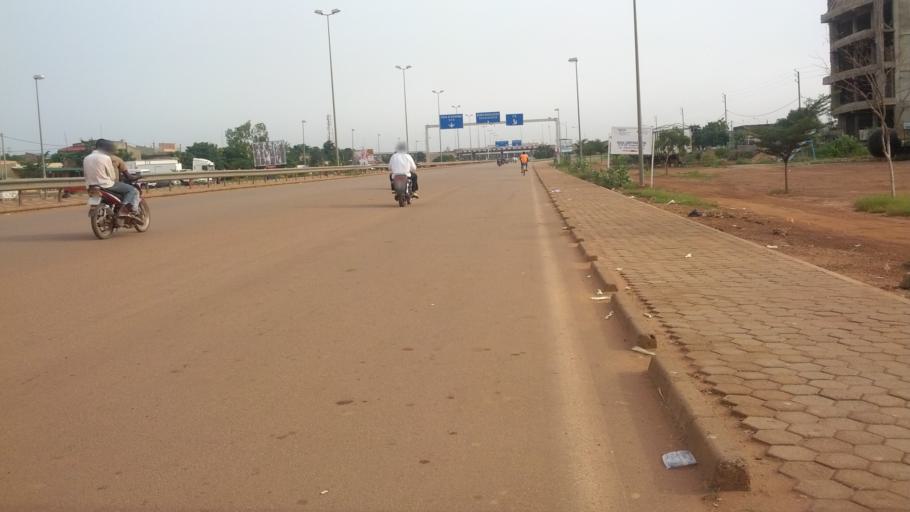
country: BF
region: Centre
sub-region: Kadiogo Province
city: Ouagadougou
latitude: 12.3275
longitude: -1.5025
